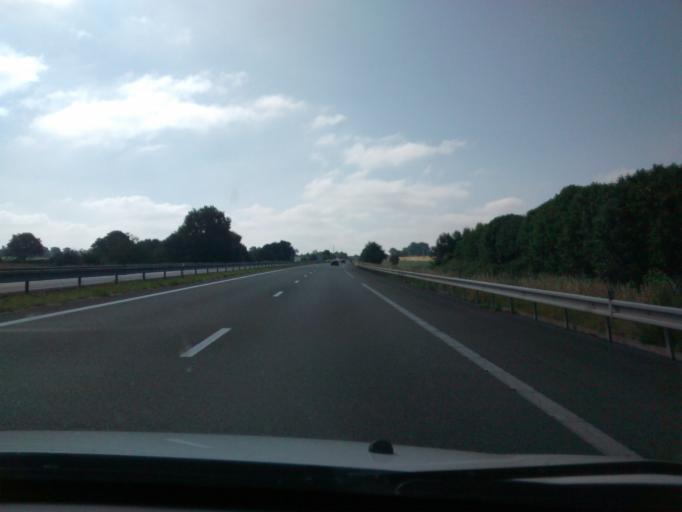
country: FR
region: Pays de la Loire
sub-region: Departement de la Mayenne
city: Bonchamp-les-Laval
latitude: 48.0926
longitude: -0.6844
